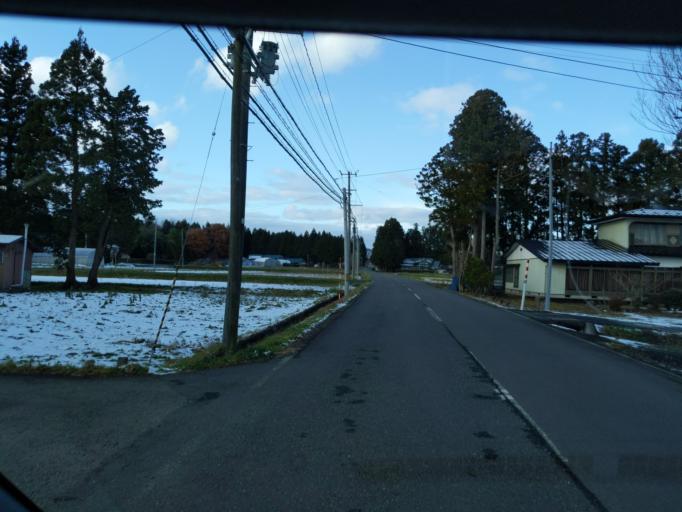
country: JP
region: Iwate
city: Kitakami
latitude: 39.2179
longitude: 141.0468
